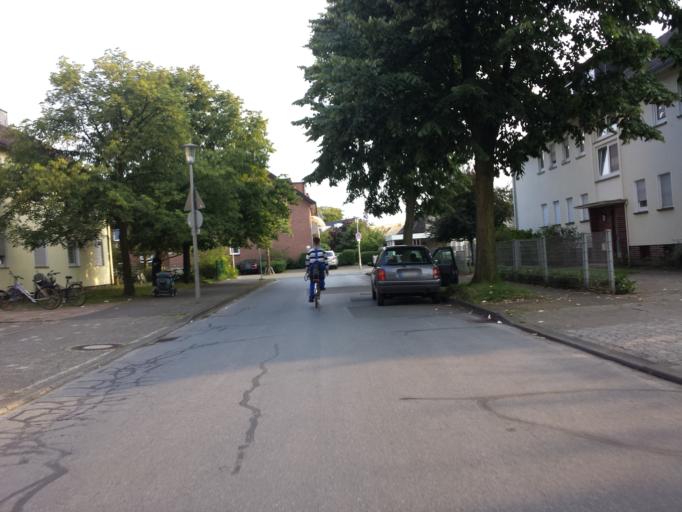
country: DE
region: North Rhine-Westphalia
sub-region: Regierungsbezirk Detmold
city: Guetersloh
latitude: 51.9056
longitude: 8.3628
